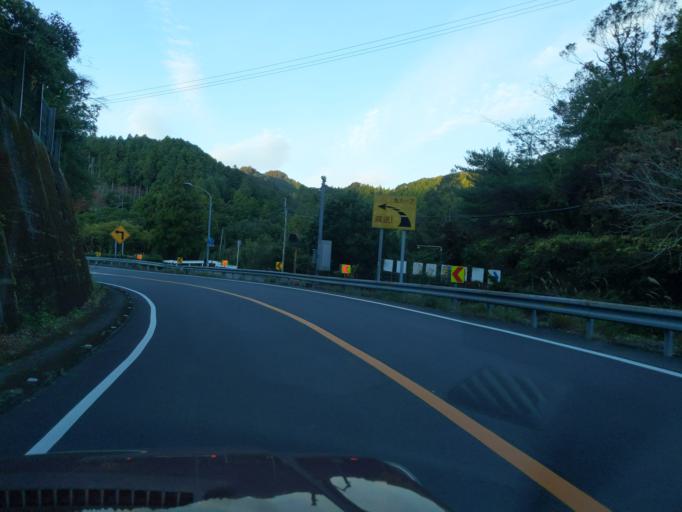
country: JP
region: Tokushima
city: Anan
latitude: 33.6990
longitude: 134.4358
